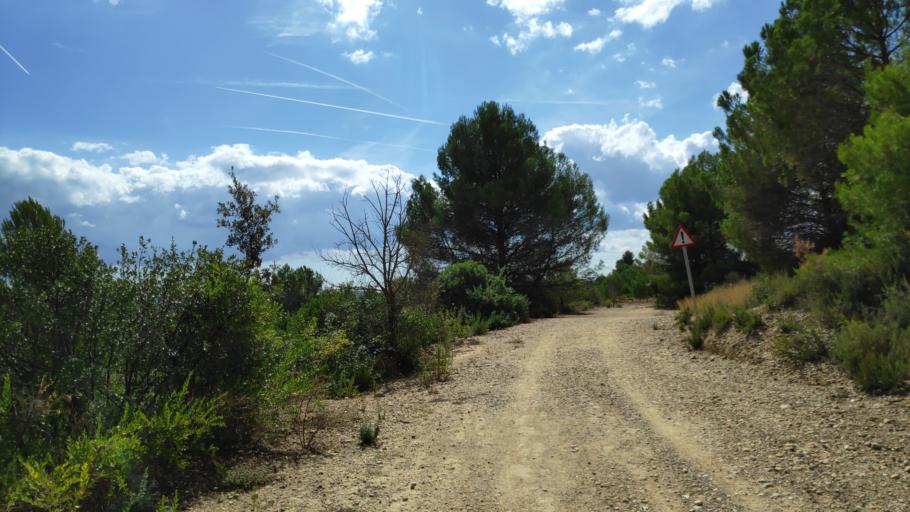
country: ES
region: Catalonia
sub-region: Provincia de Barcelona
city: Rubi
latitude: 41.5151
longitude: 2.0308
